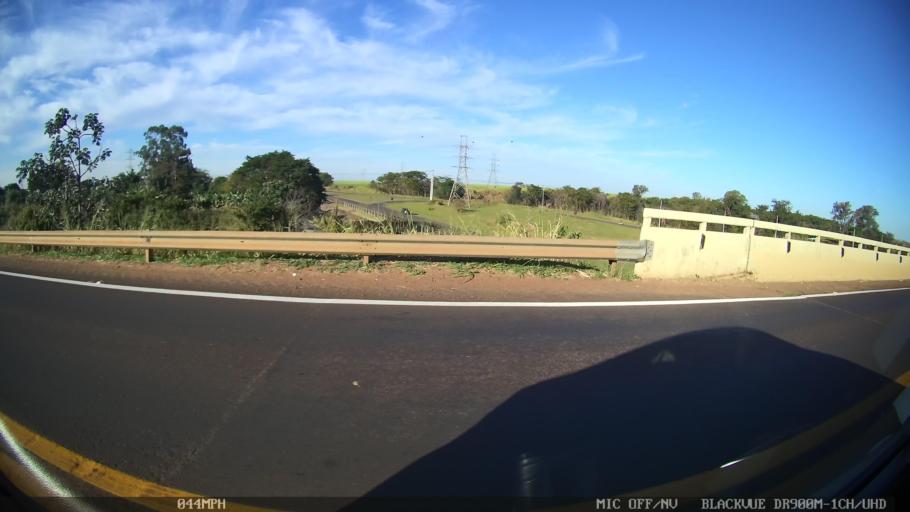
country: BR
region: Sao Paulo
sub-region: Americo Brasiliense
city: Americo Brasiliense
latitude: -21.7547
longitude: -48.1211
